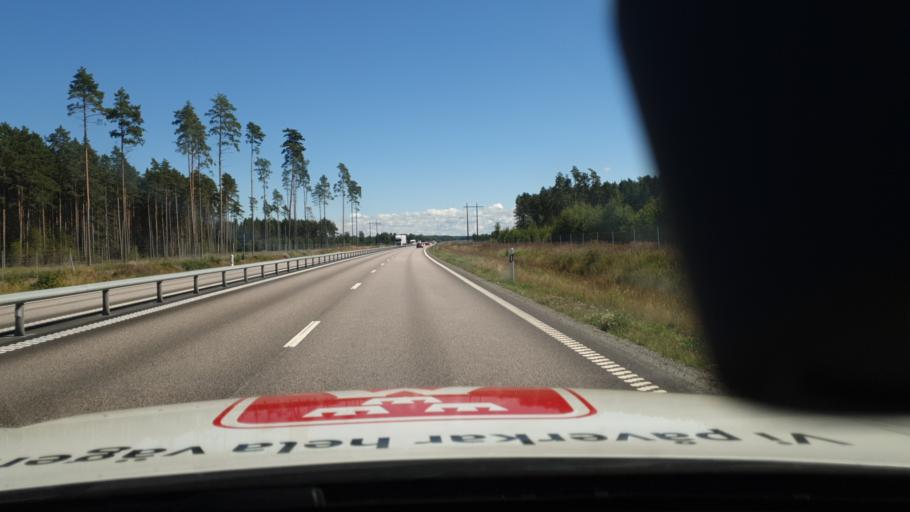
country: SE
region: Vaestra Goetaland
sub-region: Lidkopings Kommun
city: Lidkoping
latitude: 58.4796
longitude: 13.2081
